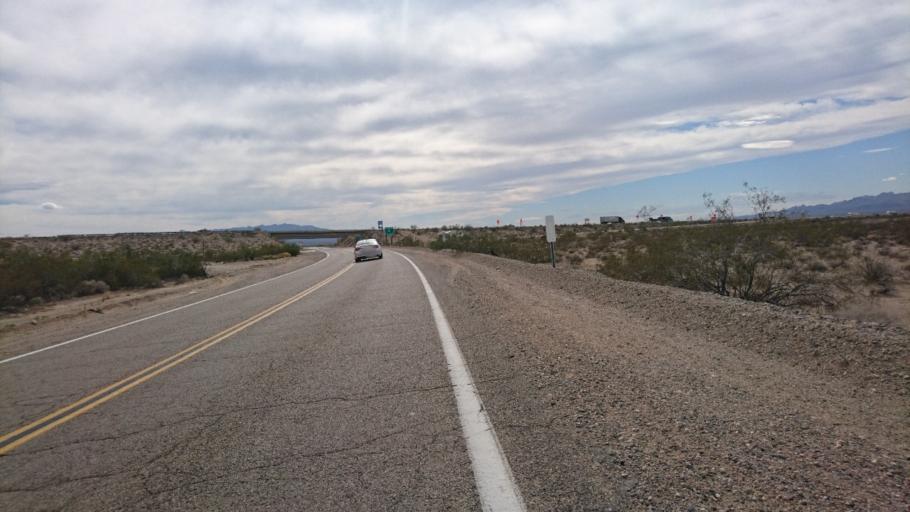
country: US
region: California
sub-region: San Bernardino County
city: Needles
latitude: 34.8144
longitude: -115.1897
